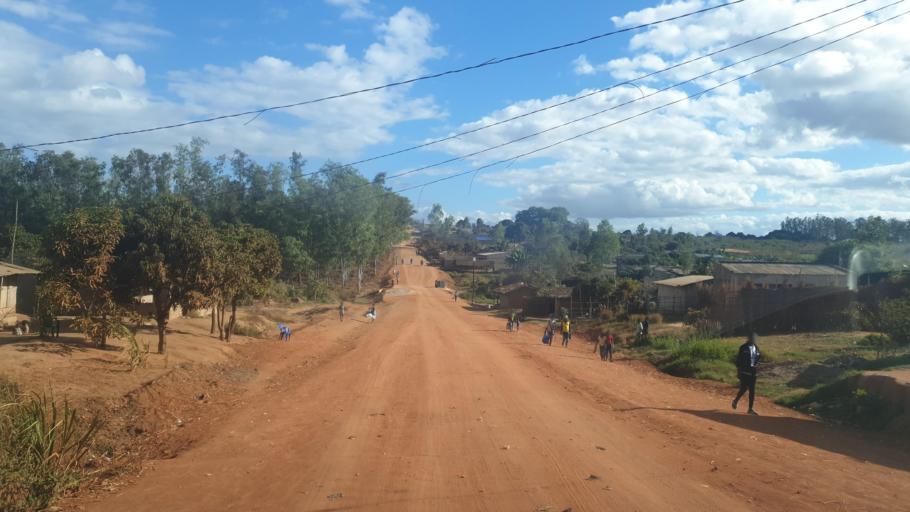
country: MZ
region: Nampula
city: Nampula
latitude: -15.0967
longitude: 39.2251
